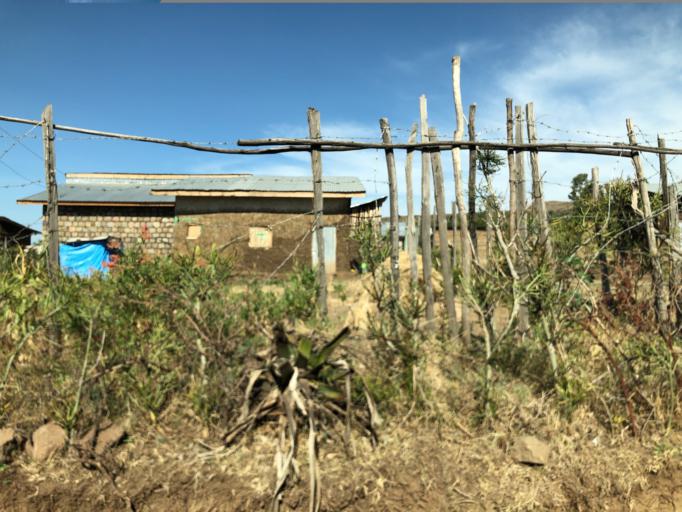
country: ET
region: Amhara
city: Lalibela
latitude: 11.9981
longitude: 39.0612
